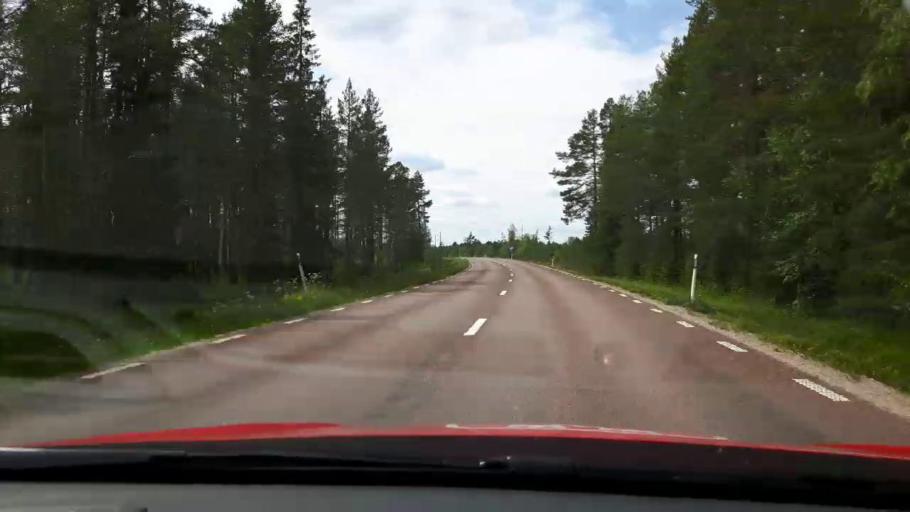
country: SE
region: Jaemtland
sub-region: Harjedalens Kommun
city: Sveg
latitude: 62.0471
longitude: 14.4818
